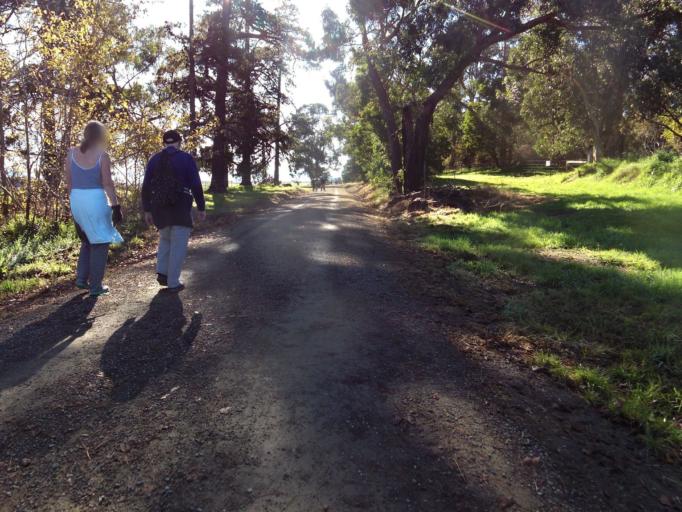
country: AU
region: Victoria
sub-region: Yarra Ranges
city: Lilydale
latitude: -37.7392
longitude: 145.3618
